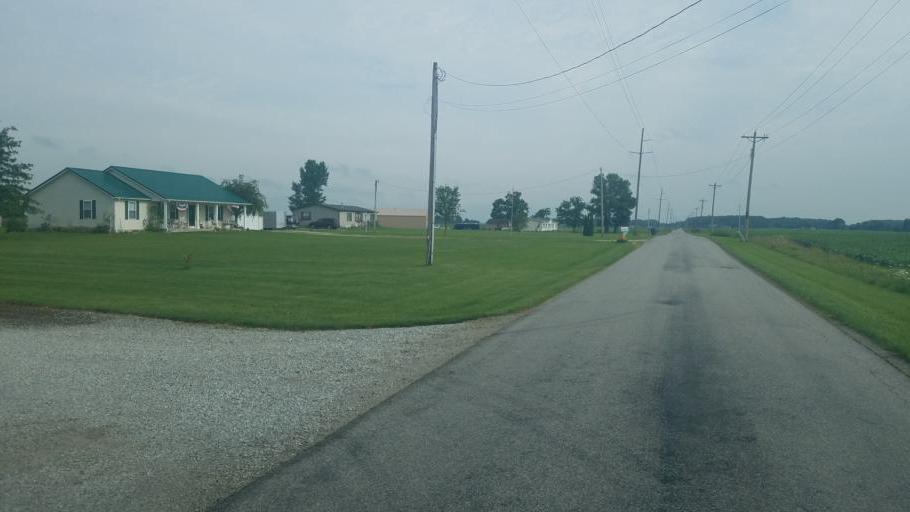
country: US
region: Ohio
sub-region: Delaware County
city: Ashley
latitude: 40.4086
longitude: -82.9104
